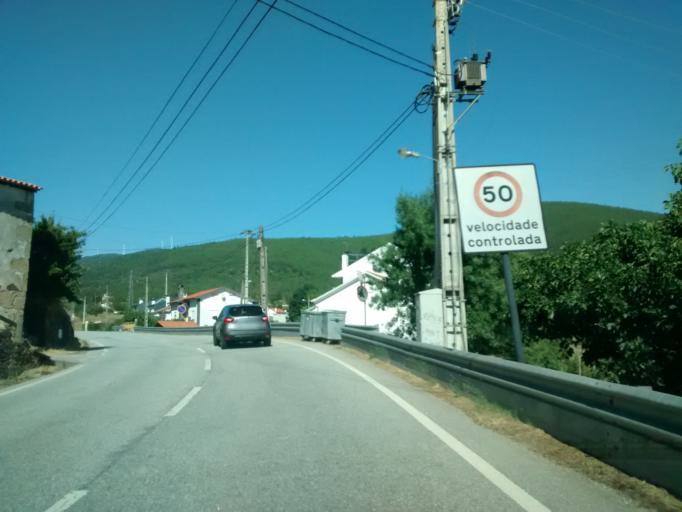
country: PT
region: Castelo Branco
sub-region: Belmonte
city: Belmonte
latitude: 40.4052
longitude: -7.4059
